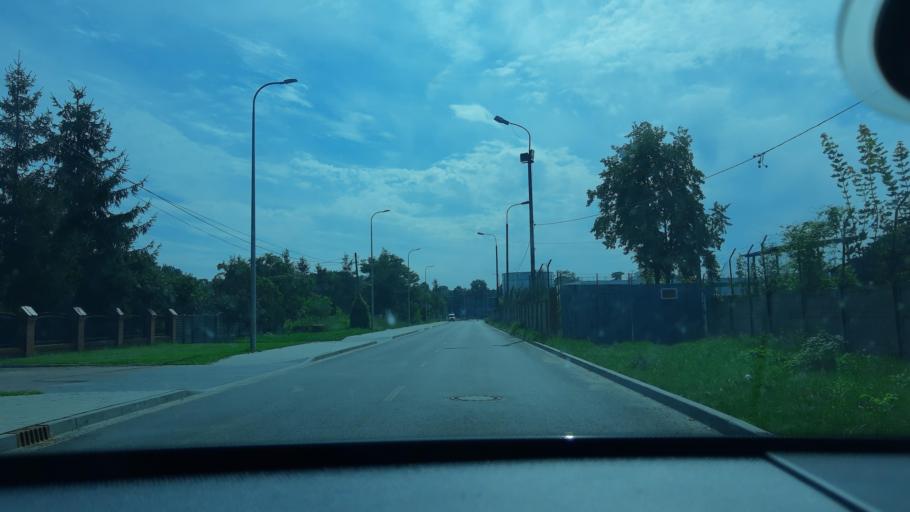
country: PL
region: Lodz Voivodeship
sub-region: Powiat sieradzki
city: Sieradz
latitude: 51.5993
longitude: 18.7290
